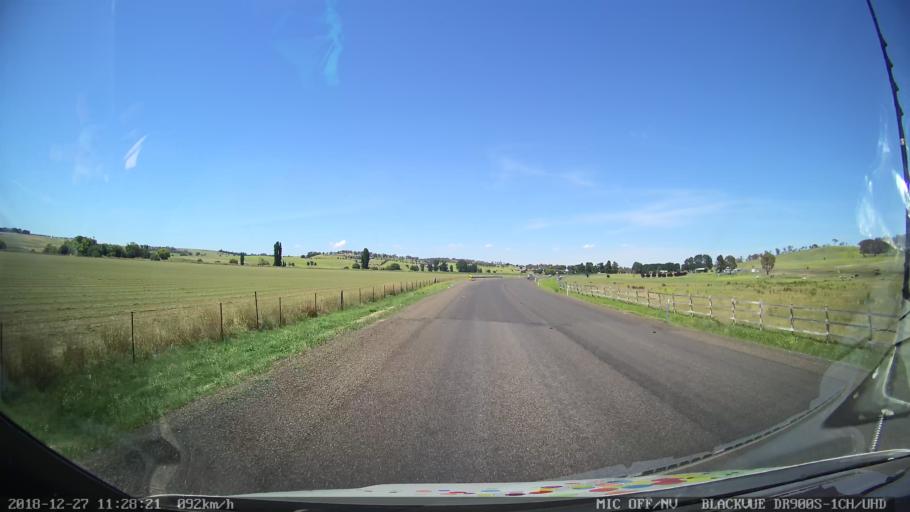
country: AU
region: New South Wales
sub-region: Bathurst Regional
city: Perthville
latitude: -33.4750
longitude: 149.5641
